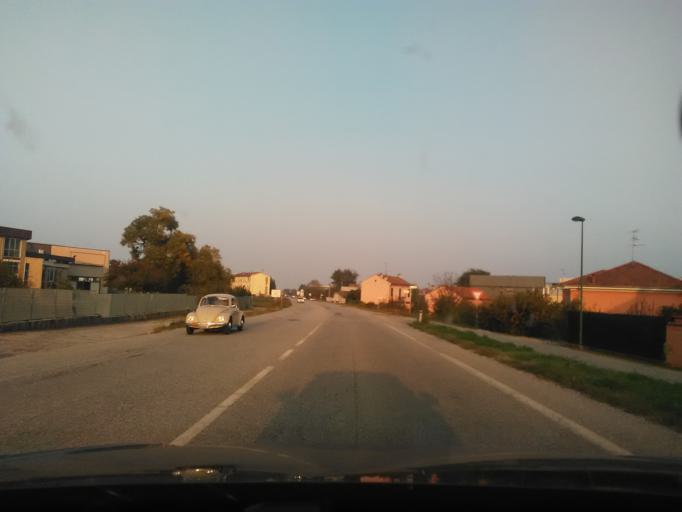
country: IT
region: Piedmont
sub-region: Provincia di Alessandria
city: Casale Monferrato
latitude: 45.1538
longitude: 8.4454
